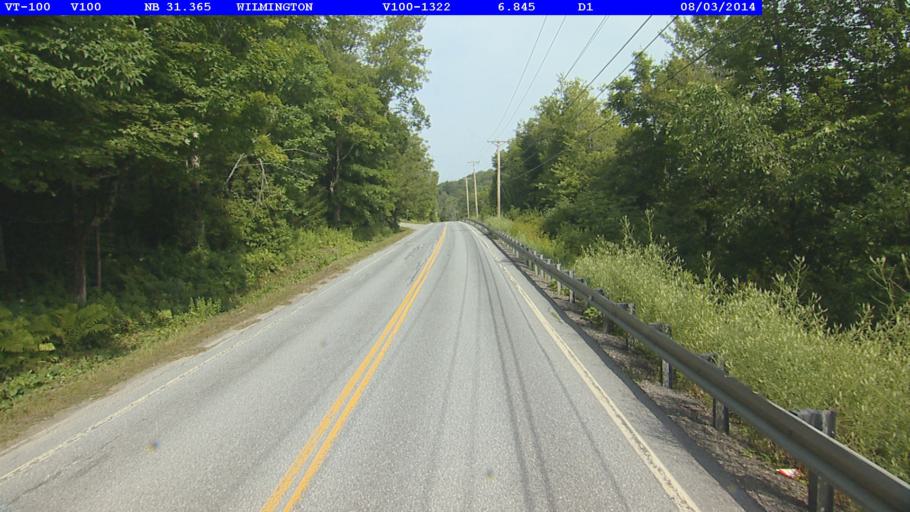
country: US
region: Vermont
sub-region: Windham County
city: Dover
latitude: 42.9197
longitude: -72.8410
